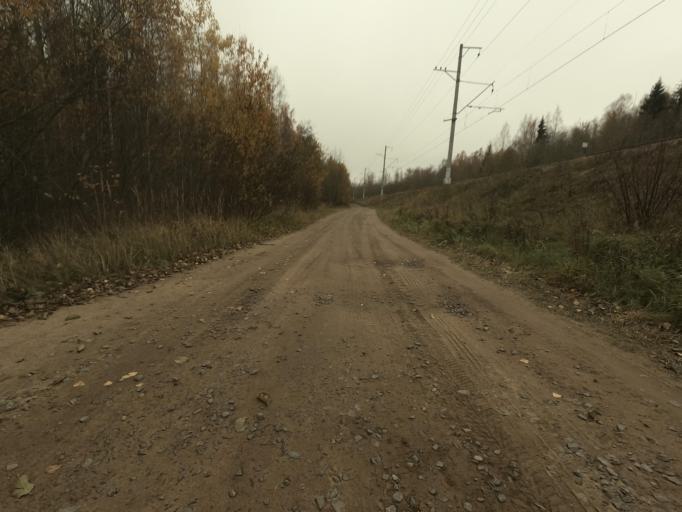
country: RU
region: Leningrad
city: Pavlovo
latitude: 59.7828
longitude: 30.8950
